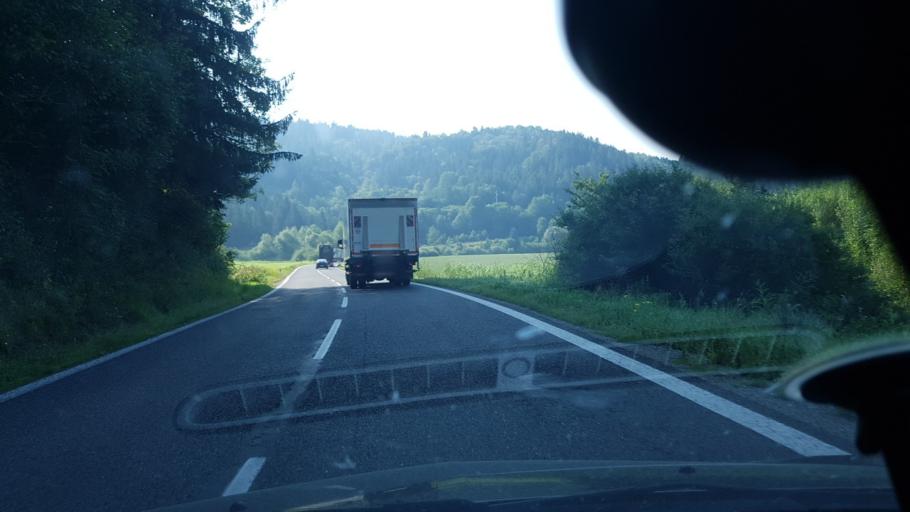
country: SK
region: Zilinsky
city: Tvrdosin
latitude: 49.2929
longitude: 19.4915
